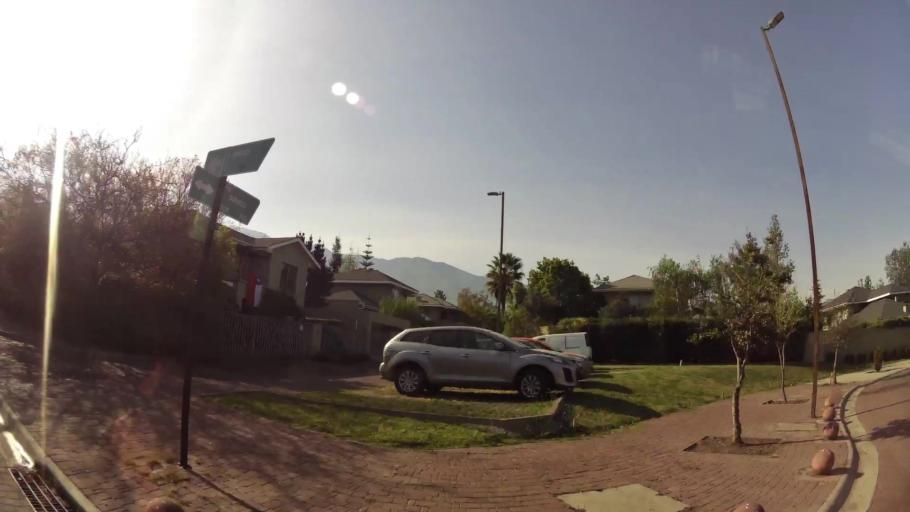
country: CL
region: Santiago Metropolitan
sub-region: Provincia de Santiago
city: Villa Presidente Frei, Nunoa, Santiago, Chile
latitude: -33.4907
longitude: -70.5536
